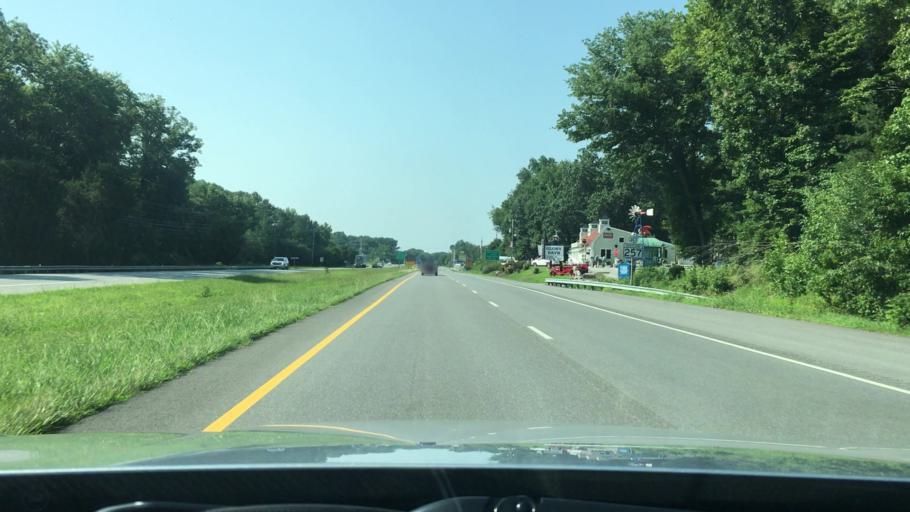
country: US
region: Virginia
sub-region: King George County
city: Dahlgren
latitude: 38.3842
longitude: -76.9562
